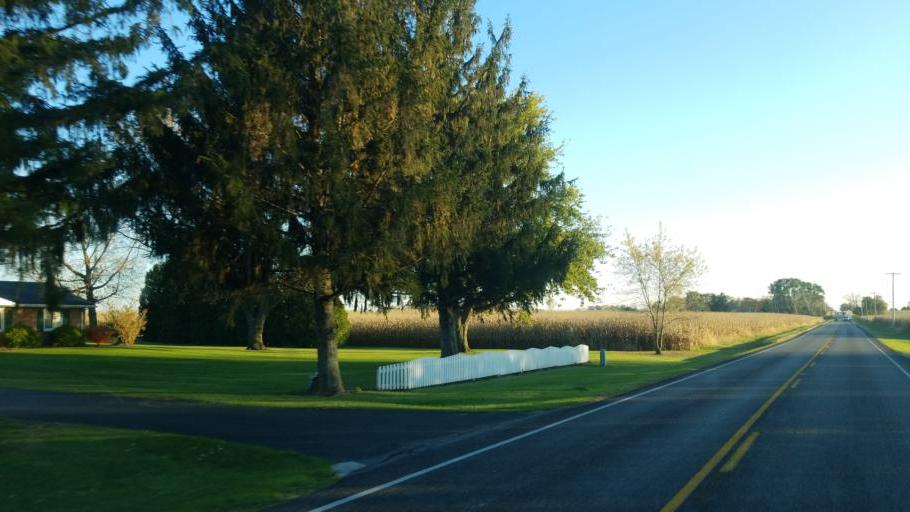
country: US
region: Ohio
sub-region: Sandusky County
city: Clyde
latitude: 41.2677
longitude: -82.9752
